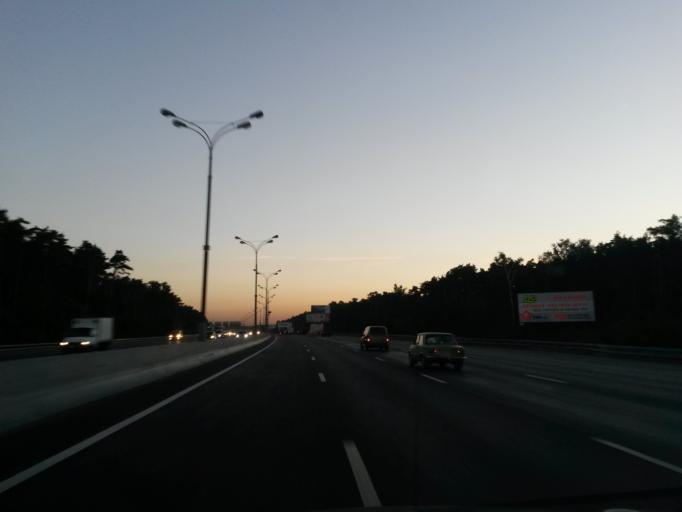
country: RU
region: Moskovskaya
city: Kotel'niki
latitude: 55.6618
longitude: 37.8397
